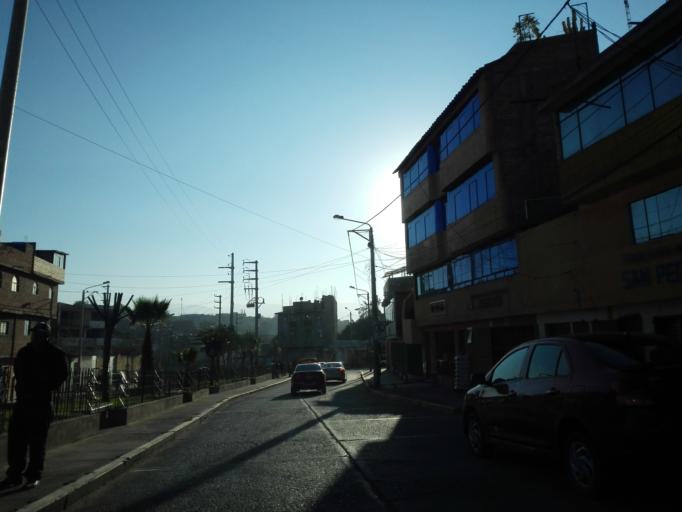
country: PE
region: Ayacucho
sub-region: Provincia de Huamanga
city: Ayacucho
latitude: -13.1636
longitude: -74.2230
